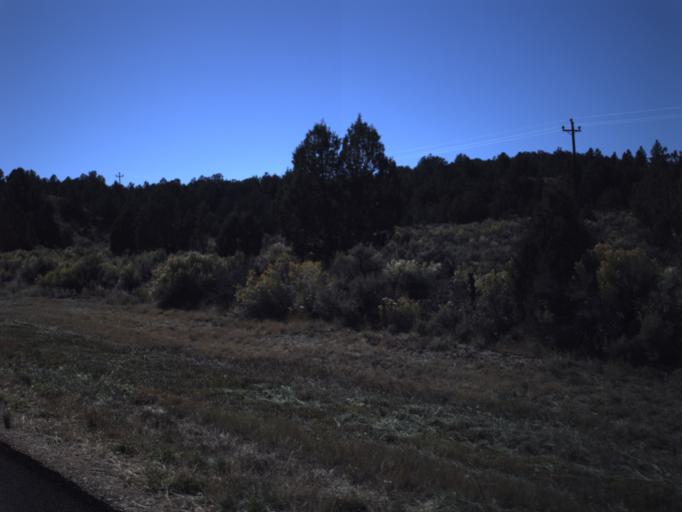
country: US
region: Utah
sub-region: Garfield County
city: Panguitch
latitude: 37.7035
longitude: -111.7902
